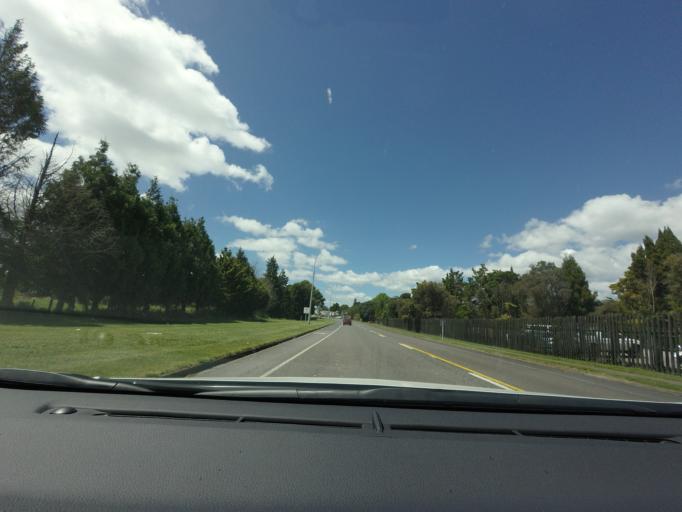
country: NZ
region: Bay of Plenty
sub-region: Rotorua District
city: Rotorua
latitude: -38.1628
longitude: 176.2511
